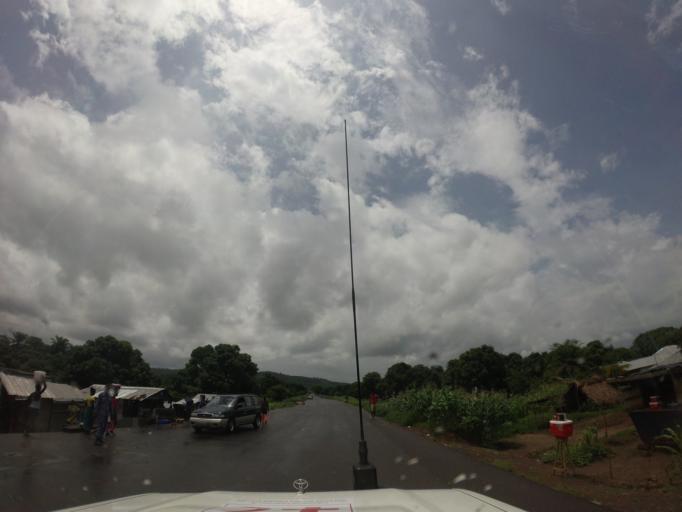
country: SL
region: Northern Province
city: Pepel
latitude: 8.4509
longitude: -12.8578
